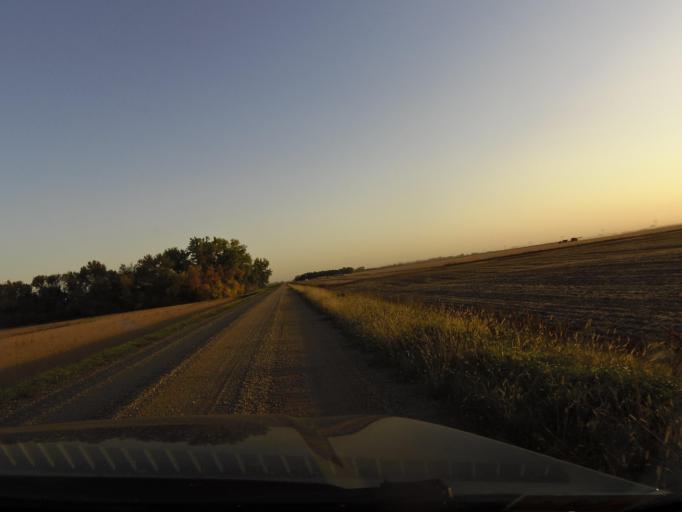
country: US
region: North Dakota
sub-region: Walsh County
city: Grafton
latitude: 48.3916
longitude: -97.2555
